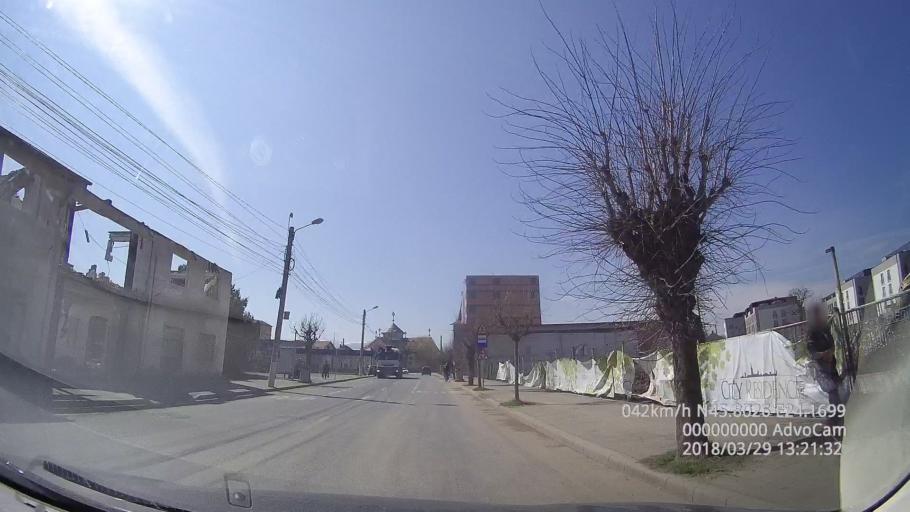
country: RO
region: Sibiu
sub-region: Municipiul Sibiu
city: Sibiu
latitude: 45.8024
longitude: 24.1698
